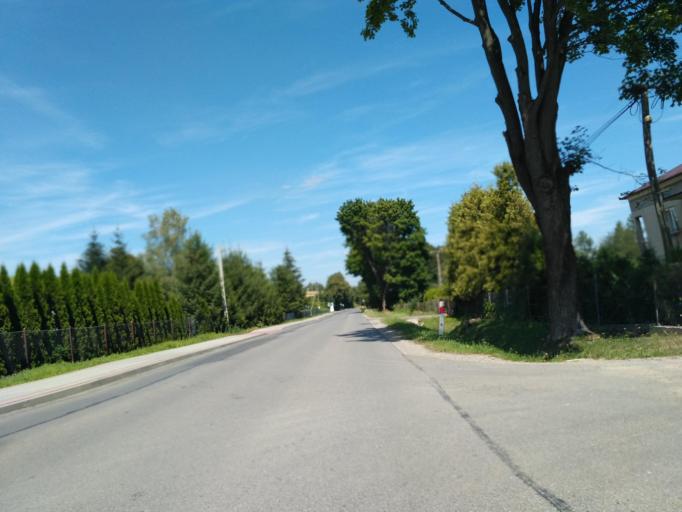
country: PL
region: Subcarpathian Voivodeship
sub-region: Powiat sanocki
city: Nowosielce-Gniewosz
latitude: 49.5292
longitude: 22.1066
